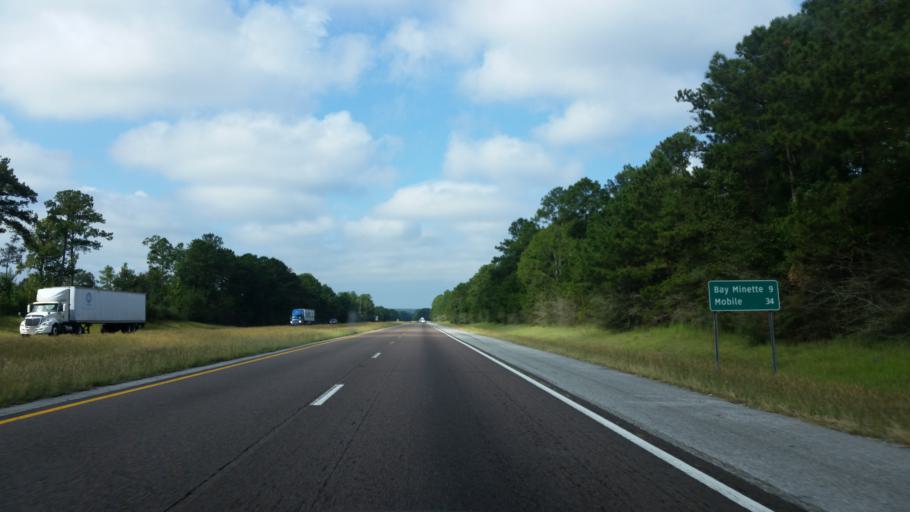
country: US
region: Alabama
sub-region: Baldwin County
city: Bay Minette
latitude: 30.9620
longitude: -87.7728
